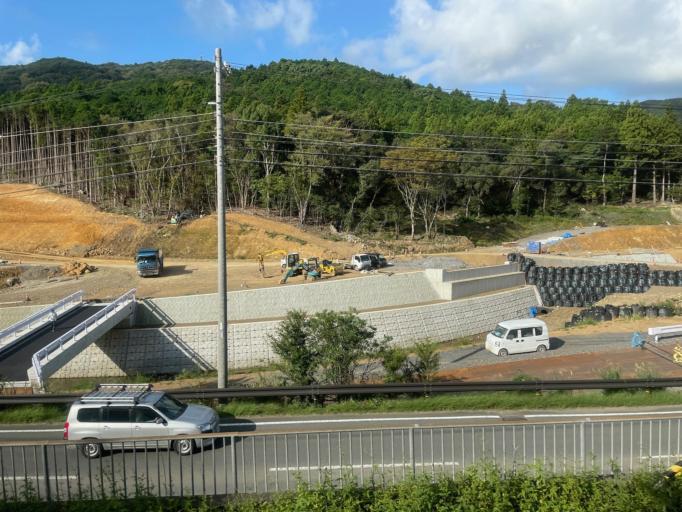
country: JP
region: Mie
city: Toba
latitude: 34.4022
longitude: 136.8095
